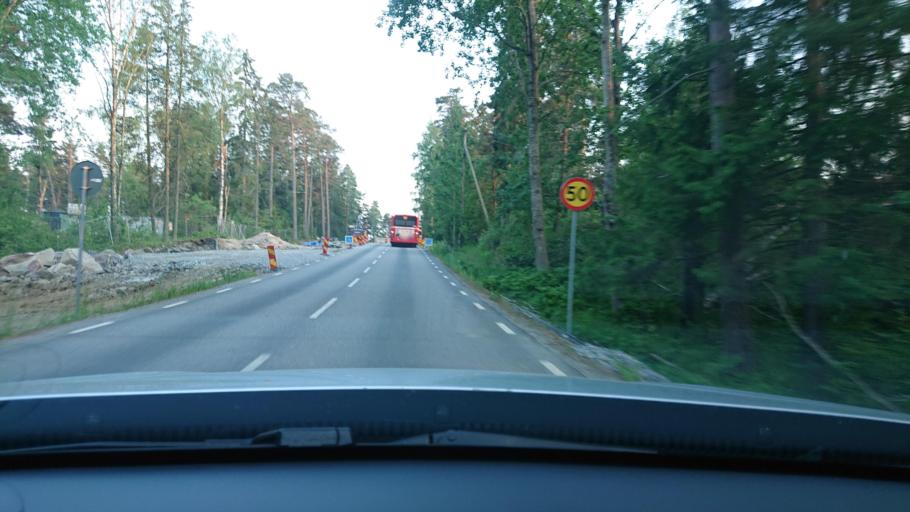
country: SE
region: Stockholm
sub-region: Vaxholms Kommun
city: Resaro
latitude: 59.4640
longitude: 18.3570
